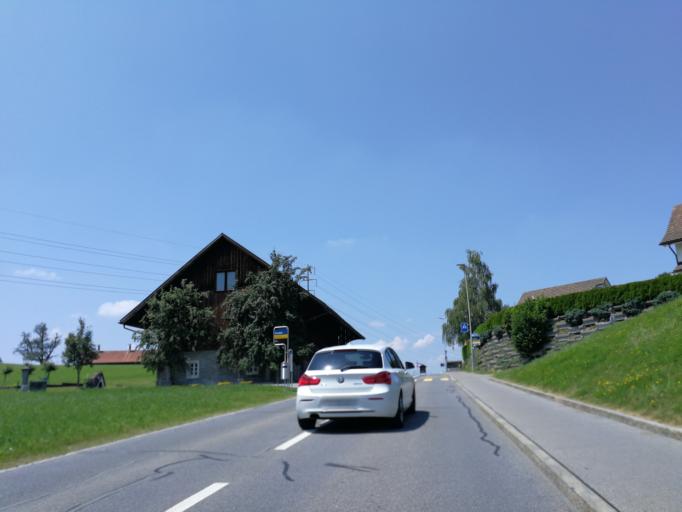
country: CH
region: Zurich
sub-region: Bezirk Horgen
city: Richterswil / Richterswil (Dorfkern)
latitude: 47.1906
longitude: 8.7013
